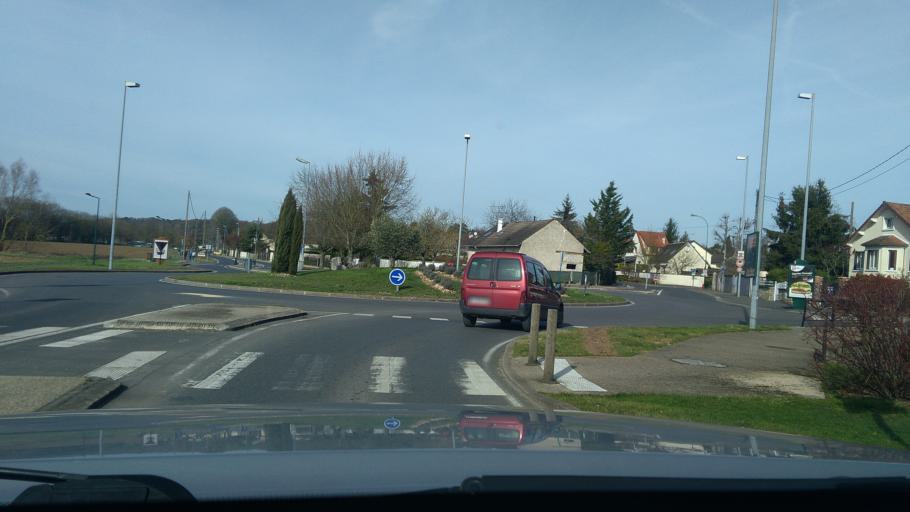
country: FR
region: Ile-de-France
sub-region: Departement de Seine-et-Marne
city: Livry-sur-Seine
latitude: 48.5194
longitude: 2.6736
